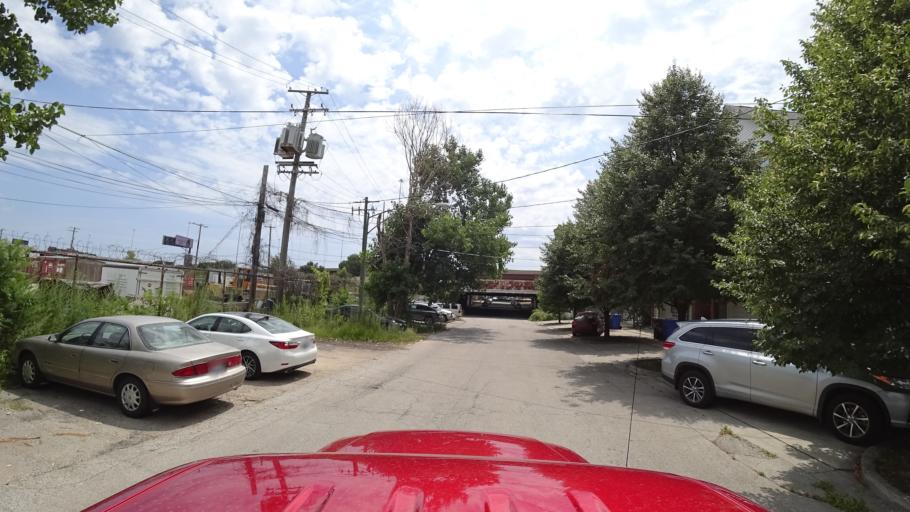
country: US
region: Illinois
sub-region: Cook County
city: Chicago
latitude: 41.8466
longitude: -87.6518
